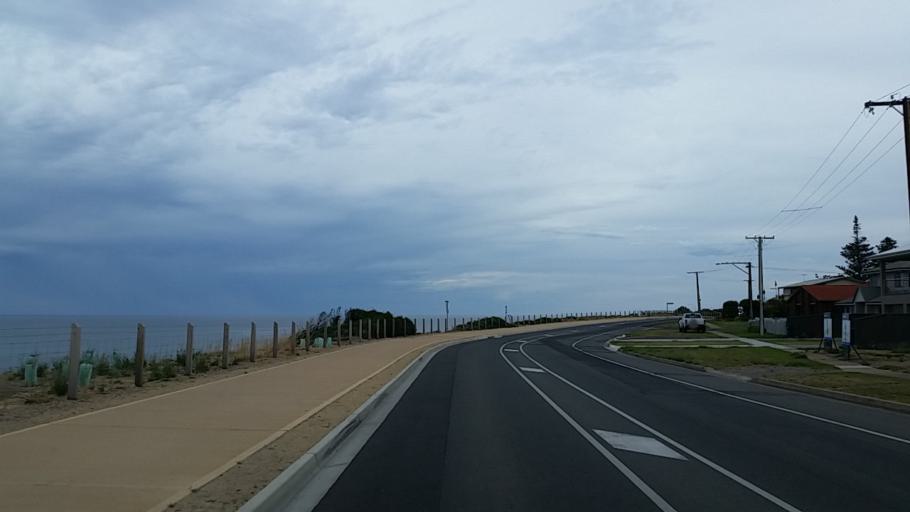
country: AU
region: South Australia
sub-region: Onkaparinga
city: Port Willunga
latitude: -35.2841
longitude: 138.4435
